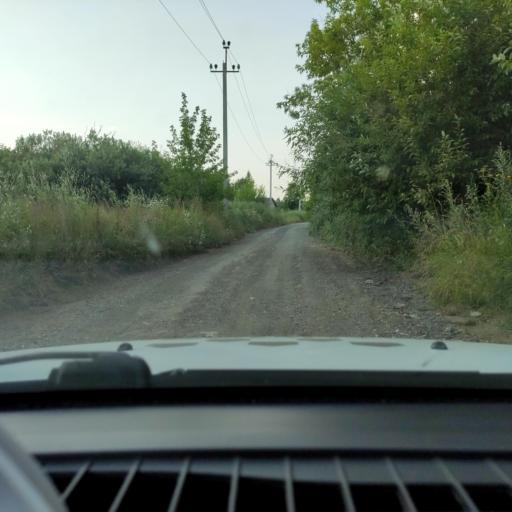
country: RU
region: Perm
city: Perm
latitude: 58.0257
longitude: 56.2107
